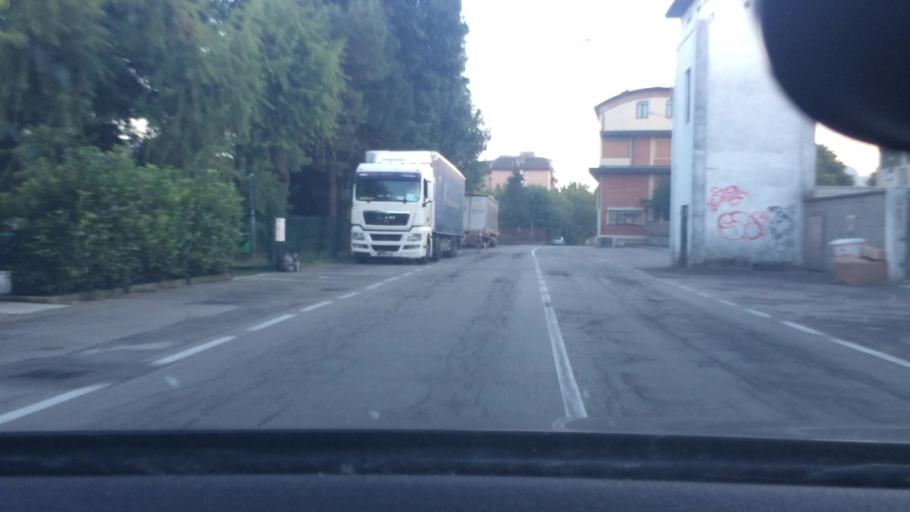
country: IT
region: Lombardy
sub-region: Citta metropolitana di Milano
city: Pogliano Milanese
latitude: 45.5435
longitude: 9.0010
